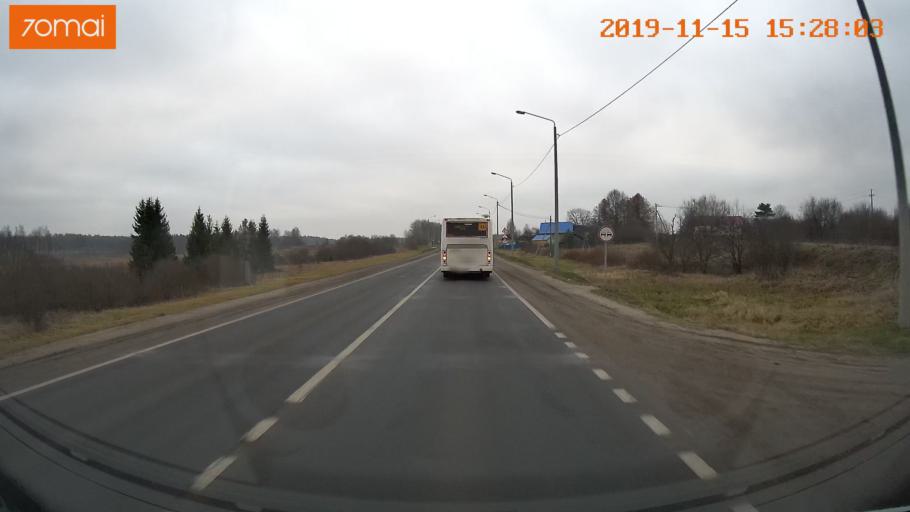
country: RU
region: Jaroslavl
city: Danilov
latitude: 58.1355
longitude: 40.1382
